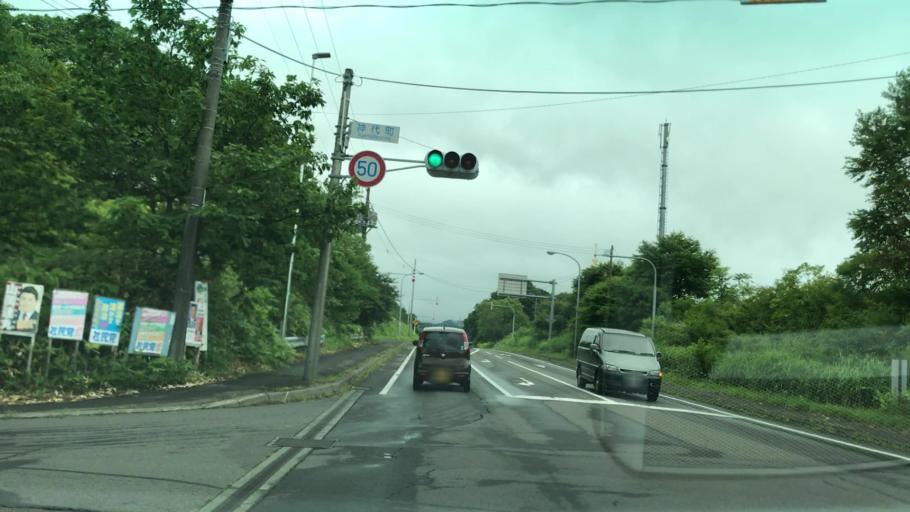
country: JP
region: Hokkaido
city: Muroran
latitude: 42.3871
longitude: 140.9847
